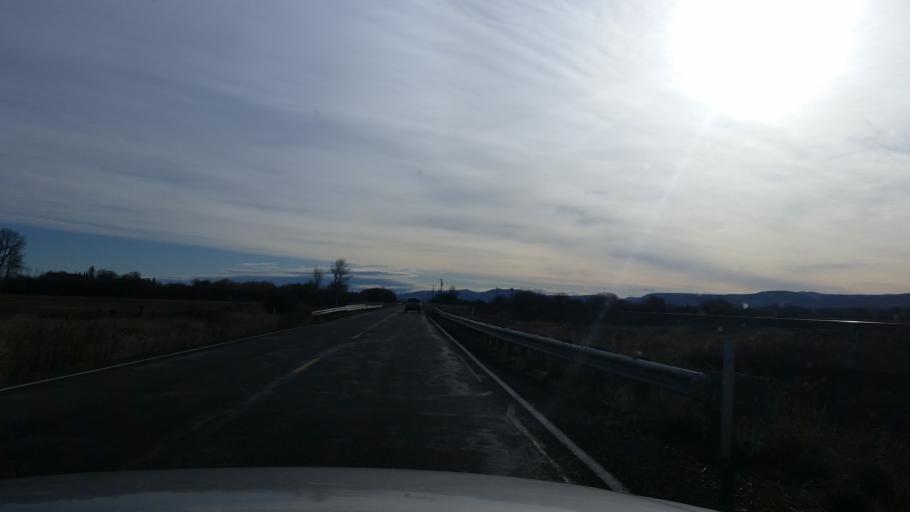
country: US
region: Washington
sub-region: Kittitas County
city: Ellensburg
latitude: 47.0388
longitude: -120.6172
